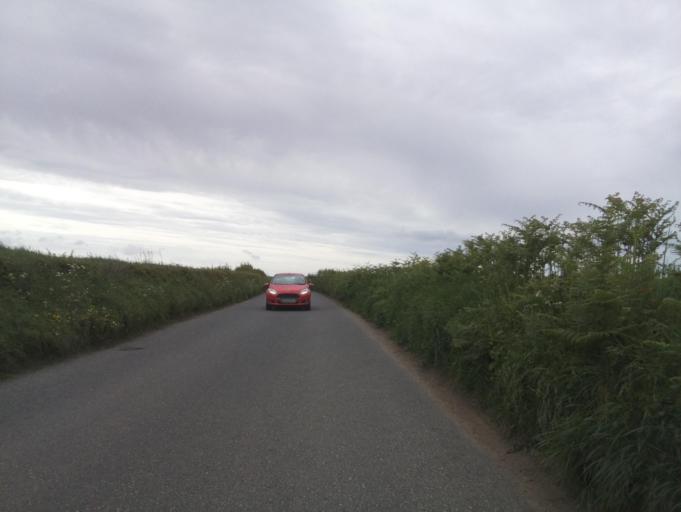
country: GB
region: England
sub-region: Devon
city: Dartmouth
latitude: 50.3389
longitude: -3.6531
